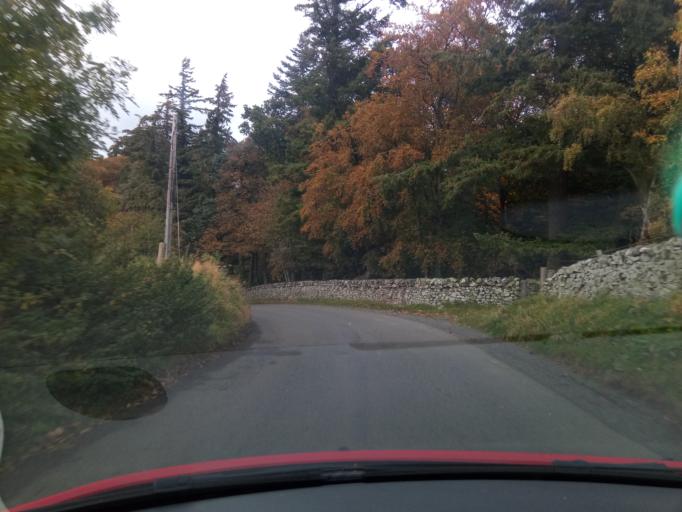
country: GB
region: Scotland
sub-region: The Scottish Borders
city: Peebles
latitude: 55.6330
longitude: -3.1420
